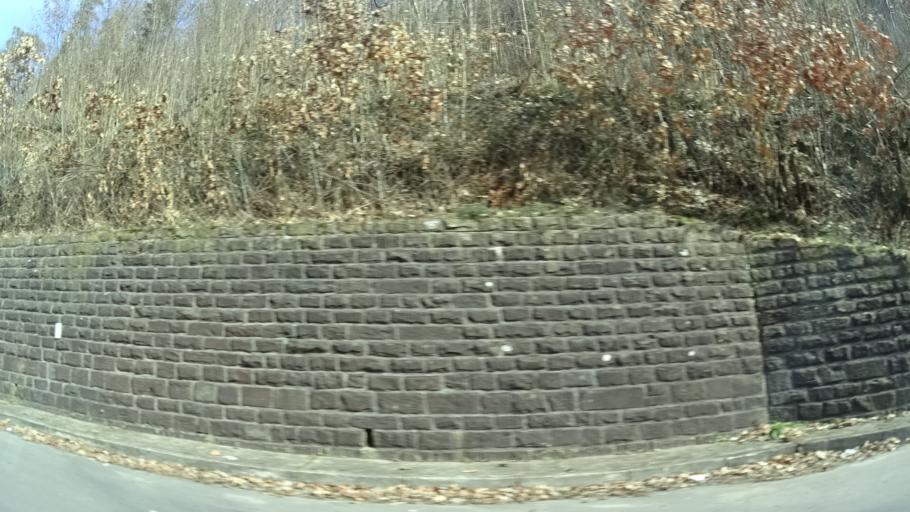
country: DE
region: Baden-Wuerttemberg
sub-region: Karlsruhe Region
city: Schonau
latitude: 49.4199
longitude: 8.8082
